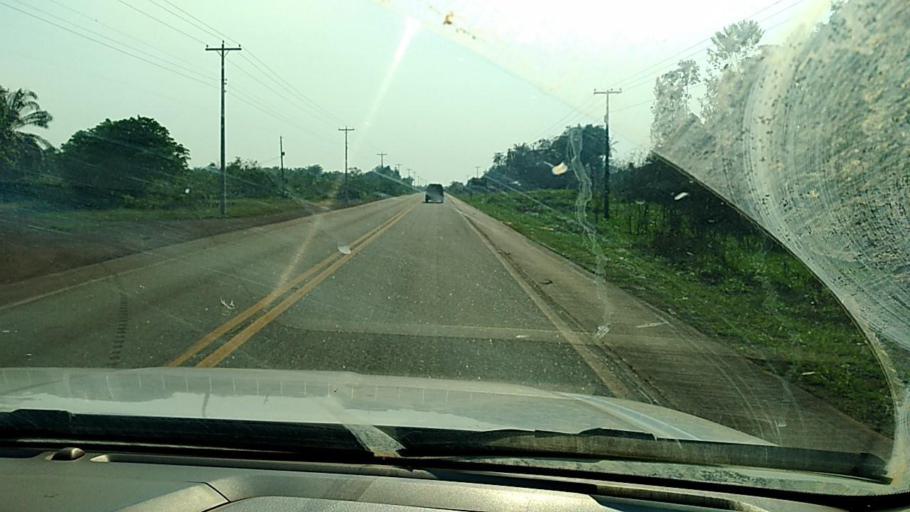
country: BR
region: Rondonia
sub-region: Porto Velho
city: Porto Velho
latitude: -8.2043
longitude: -63.8878
